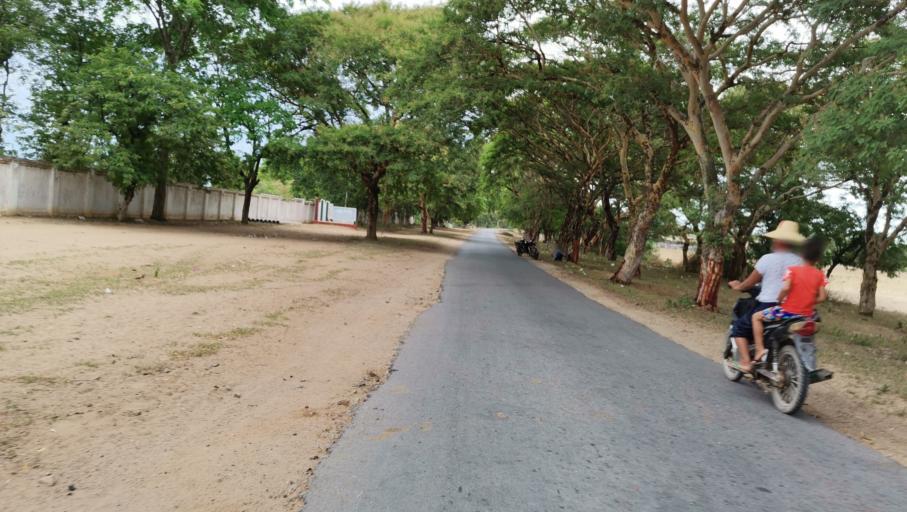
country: MM
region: Mandalay
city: Myingyan
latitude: 21.8475
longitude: 95.4295
